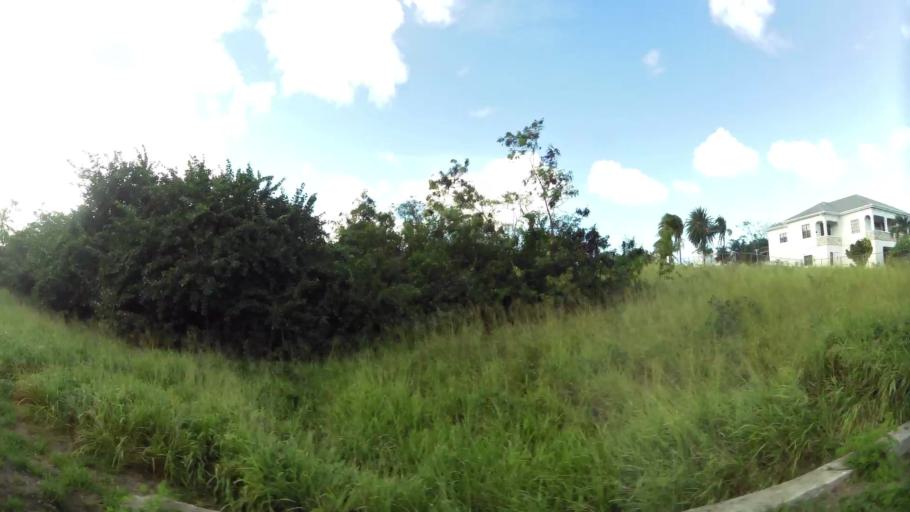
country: AG
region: Saint Peter
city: All Saints
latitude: 17.0761
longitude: -61.7836
